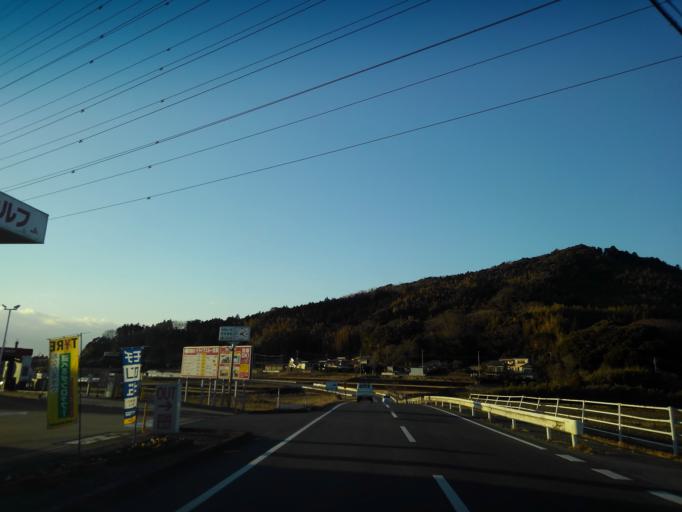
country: JP
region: Chiba
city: Kisarazu
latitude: 35.3055
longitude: 139.9855
